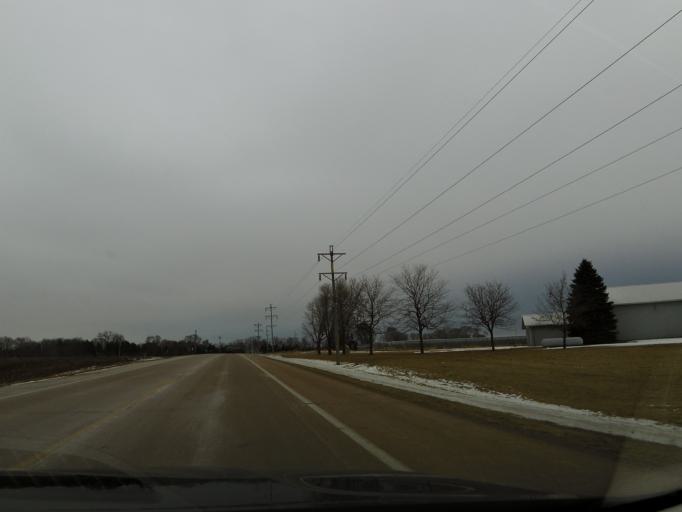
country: US
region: Minnesota
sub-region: Carver County
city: Watertown
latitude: 44.9391
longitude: -93.8300
